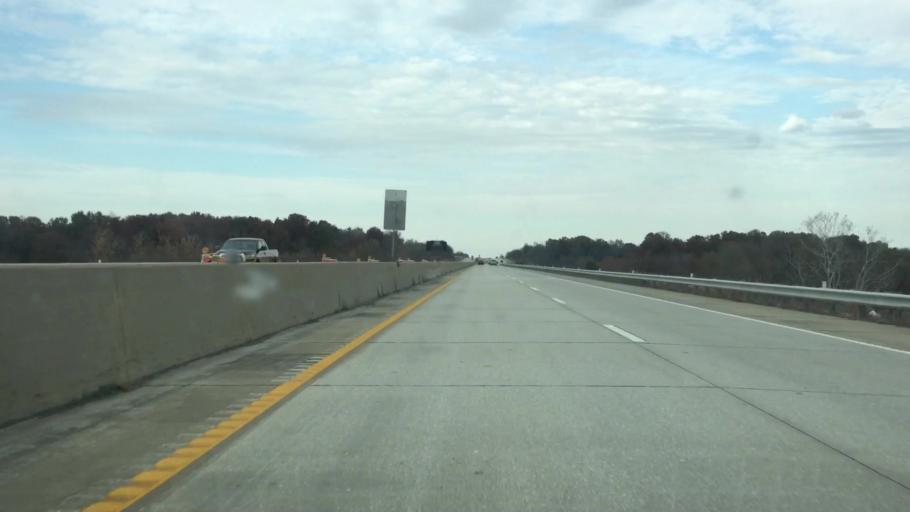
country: US
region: Missouri
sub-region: Henry County
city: Clinton
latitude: 38.2885
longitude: -93.7592
